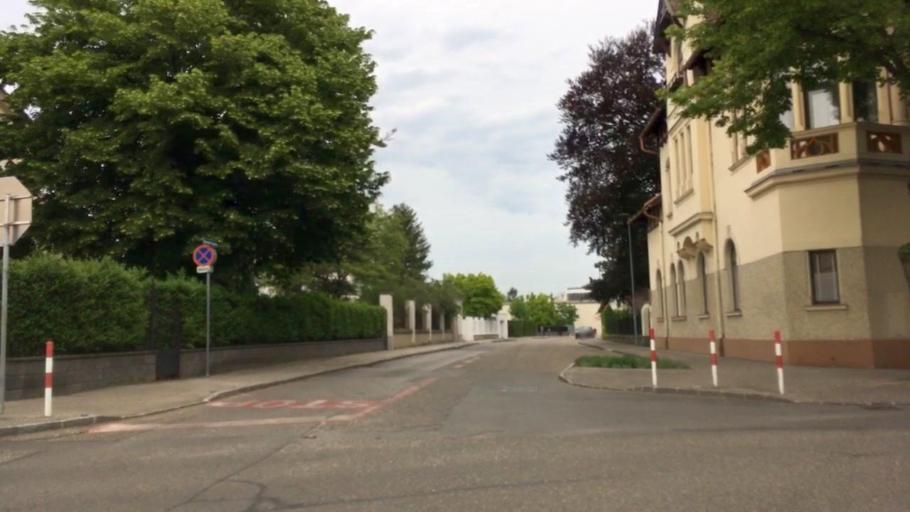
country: AT
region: Lower Austria
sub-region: Politischer Bezirk Korneuburg
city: Stockerau
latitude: 48.3892
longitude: 16.2063
